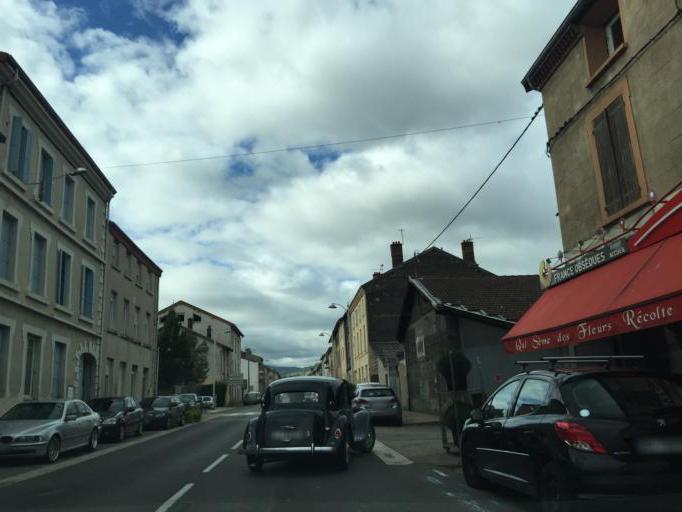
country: FR
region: Rhone-Alpes
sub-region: Departement de la Loire
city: Lorette
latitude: 45.5009
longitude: 4.5670
